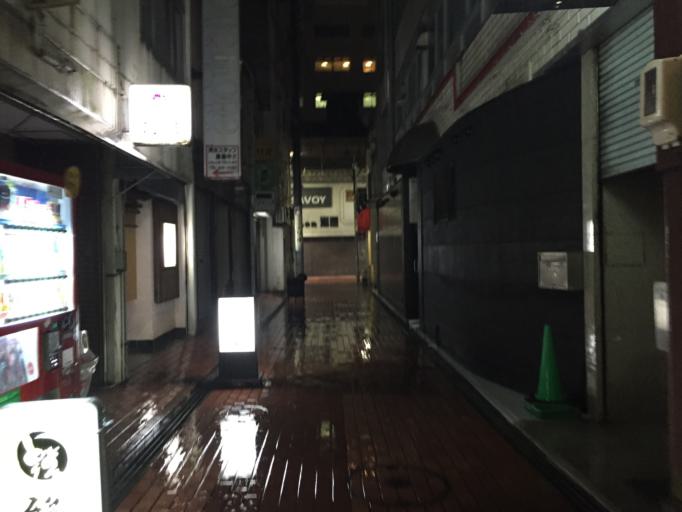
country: JP
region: Mie
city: Yokkaichi
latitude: 34.9675
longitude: 136.6221
